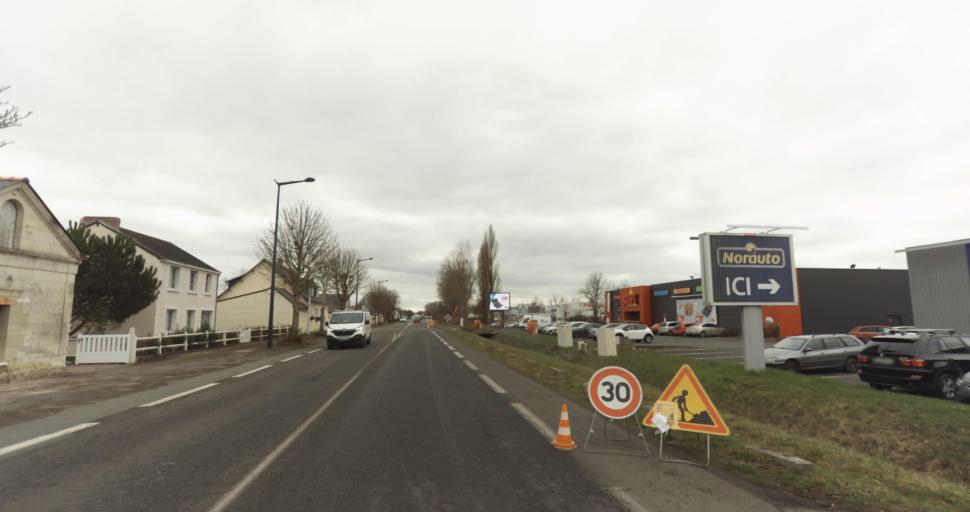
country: FR
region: Pays de la Loire
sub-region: Departement de Maine-et-Loire
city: Saumur
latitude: 47.2804
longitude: -0.0548
